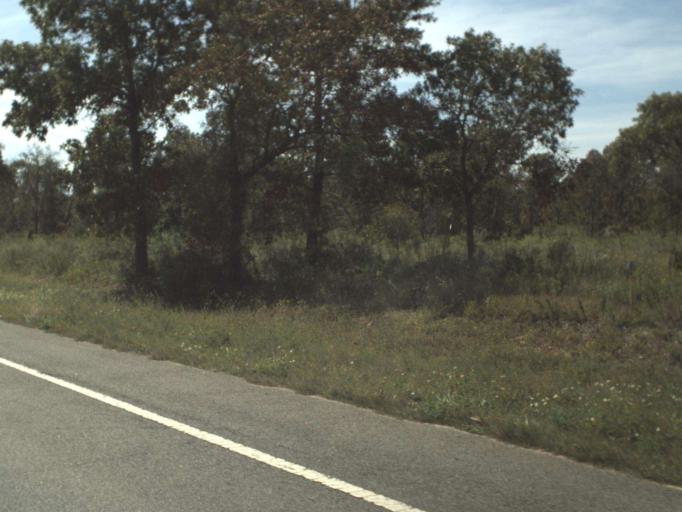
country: US
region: Florida
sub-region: Washington County
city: Chipley
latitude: 30.5806
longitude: -85.5943
